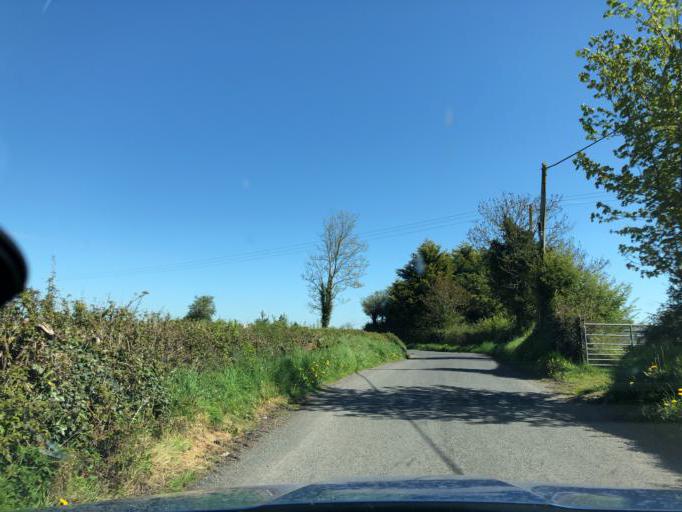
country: IE
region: Connaught
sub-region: County Galway
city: Portumna
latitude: 53.1549
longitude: -8.2952
